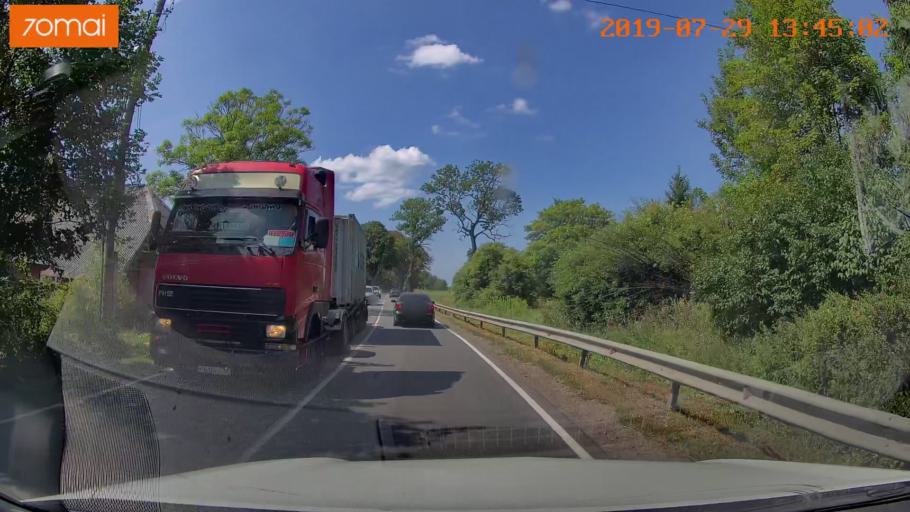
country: RU
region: Kaliningrad
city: Primorsk
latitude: 54.7393
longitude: 20.0801
